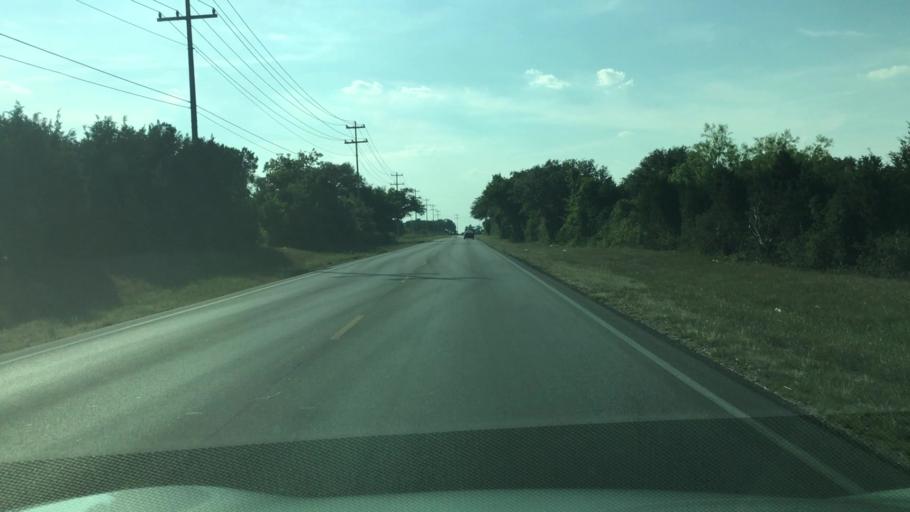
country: US
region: Texas
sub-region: Hays County
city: Buda
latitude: 30.0983
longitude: -97.9331
